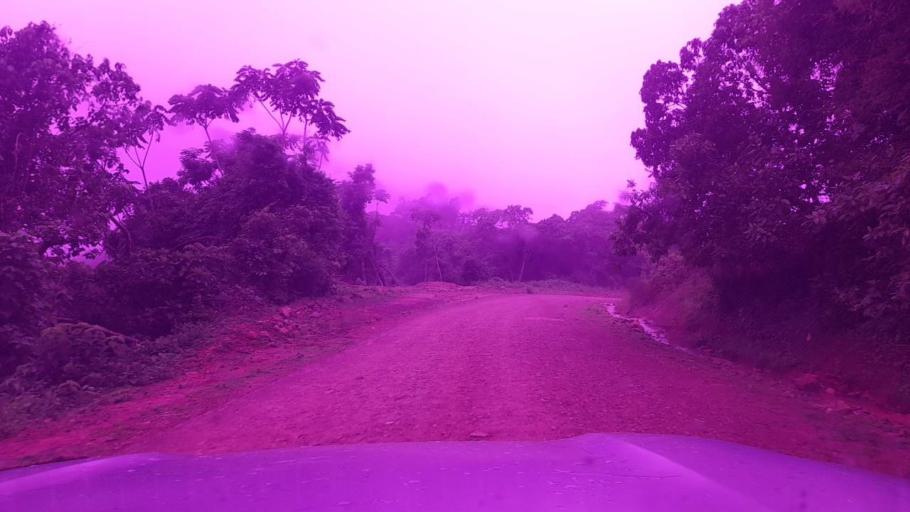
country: ET
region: Southern Nations, Nationalities, and People's Region
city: Bonga
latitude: 7.5185
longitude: 36.0578
